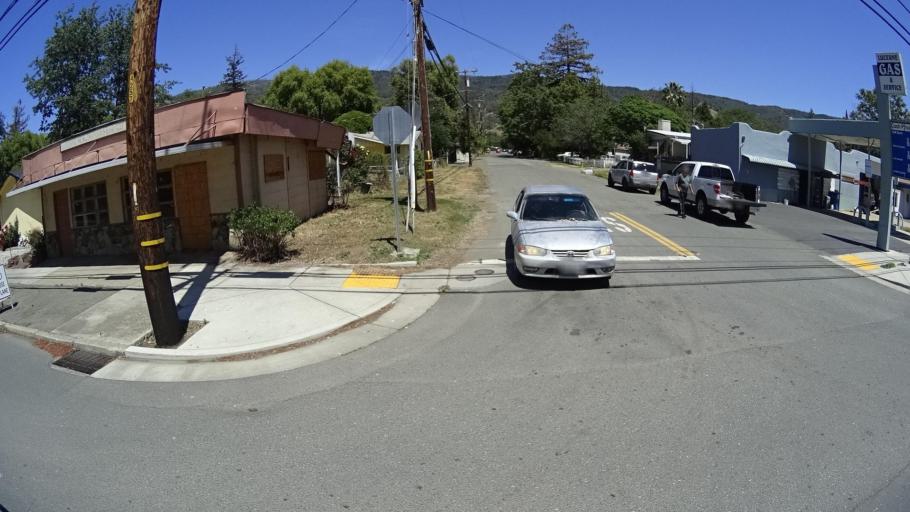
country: US
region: California
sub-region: Lake County
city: Lucerne
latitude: 39.0951
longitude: -122.8007
